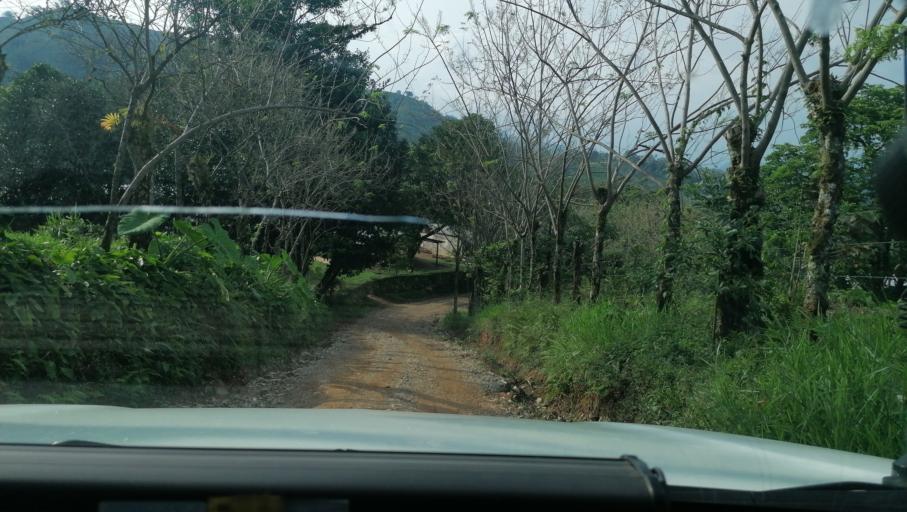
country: MX
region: Chiapas
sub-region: Tapilula
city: San Francisco Jacona
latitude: 17.3265
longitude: -93.0996
